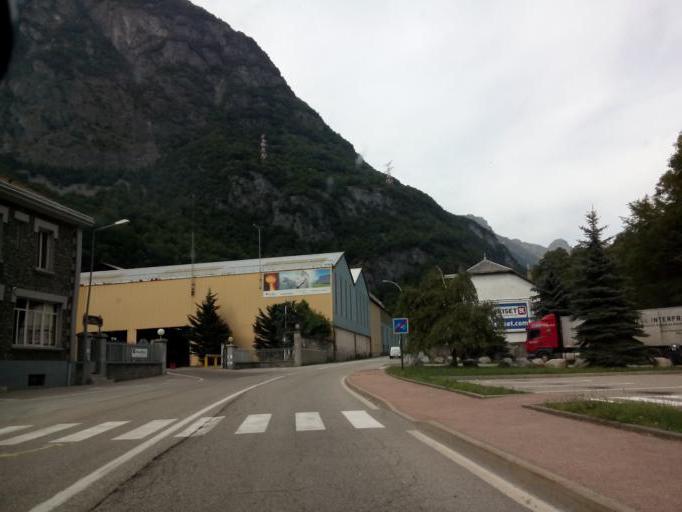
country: FR
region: Rhone-Alpes
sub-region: Departement de l'Isere
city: Vaulnaveys-le-Bas
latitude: 45.0725
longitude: 5.8759
